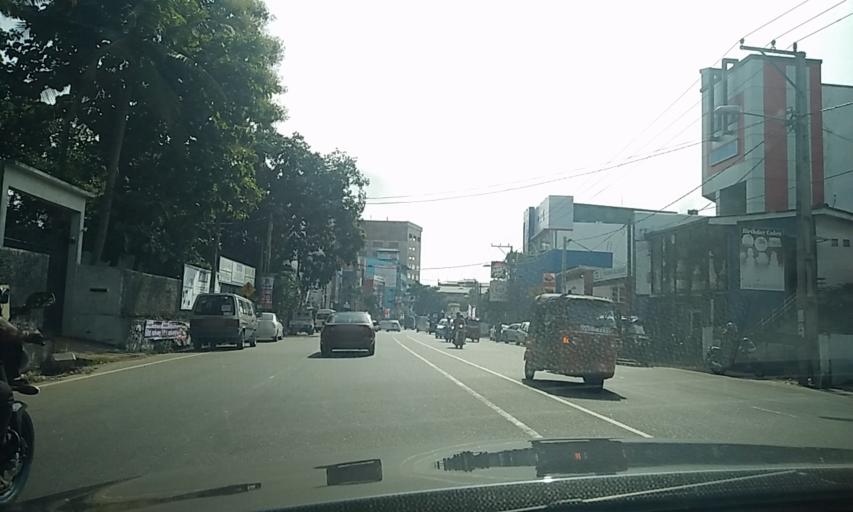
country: LK
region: Western
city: Maharagama
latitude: 6.8447
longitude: 79.9319
